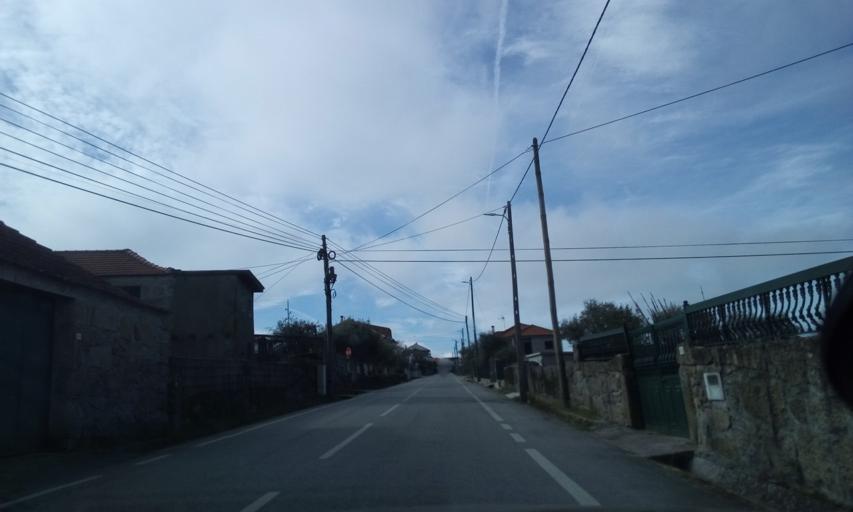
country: PT
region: Guarda
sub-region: Aguiar da Beira
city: Aguiar da Beira
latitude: 40.7625
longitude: -7.5404
